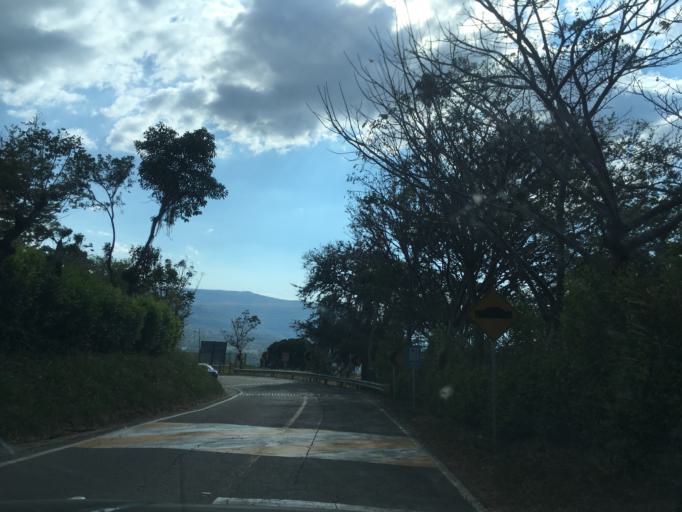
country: CO
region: Santander
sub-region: San Gil
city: San Gil
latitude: 6.5725
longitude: -73.1494
